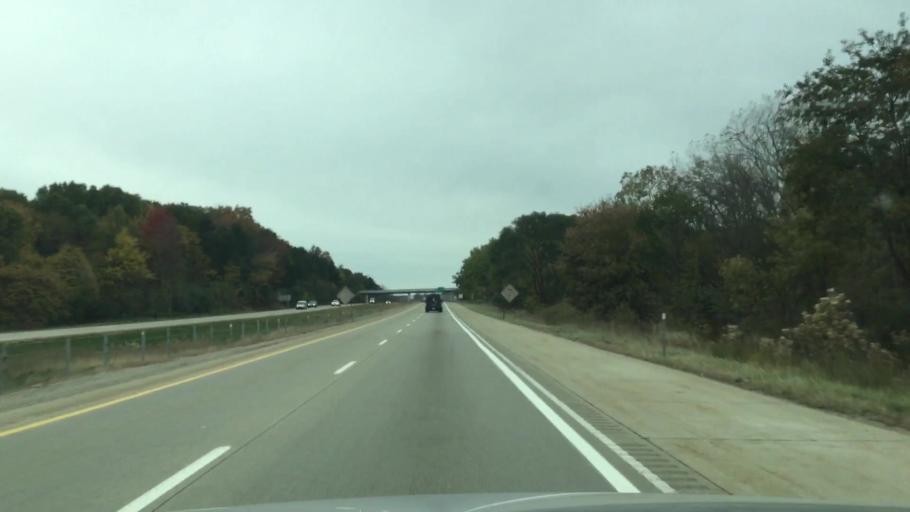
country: US
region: Michigan
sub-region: Jackson County
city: Michigan Center
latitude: 42.2865
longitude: -84.2797
